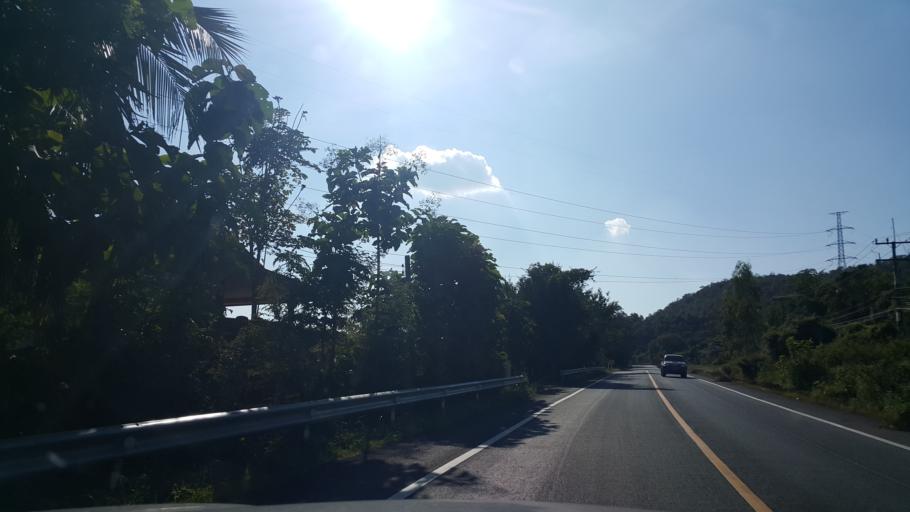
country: TH
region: Lamphun
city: Mae Tha
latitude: 18.4751
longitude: 99.1675
